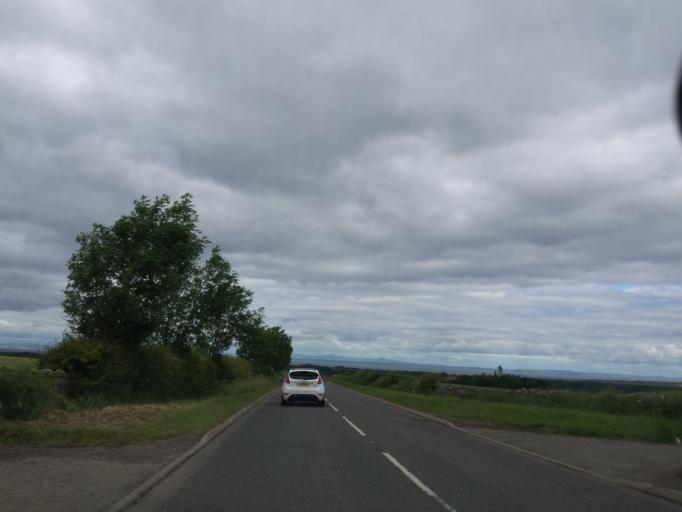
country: GB
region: Scotland
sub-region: East Lothian
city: Haddington
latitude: 55.9820
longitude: -2.8215
